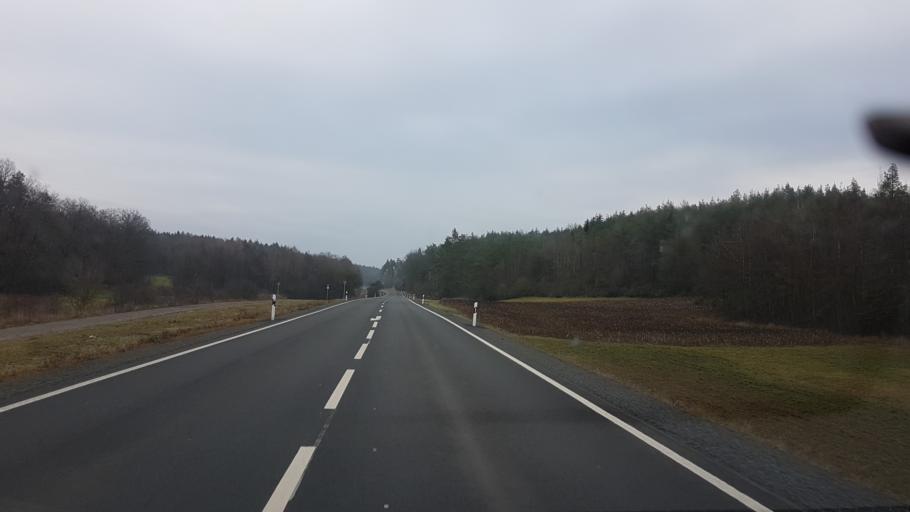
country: DE
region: Bavaria
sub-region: Regierungsbezirk Unterfranken
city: Ermershausen
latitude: 50.2289
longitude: 10.5754
